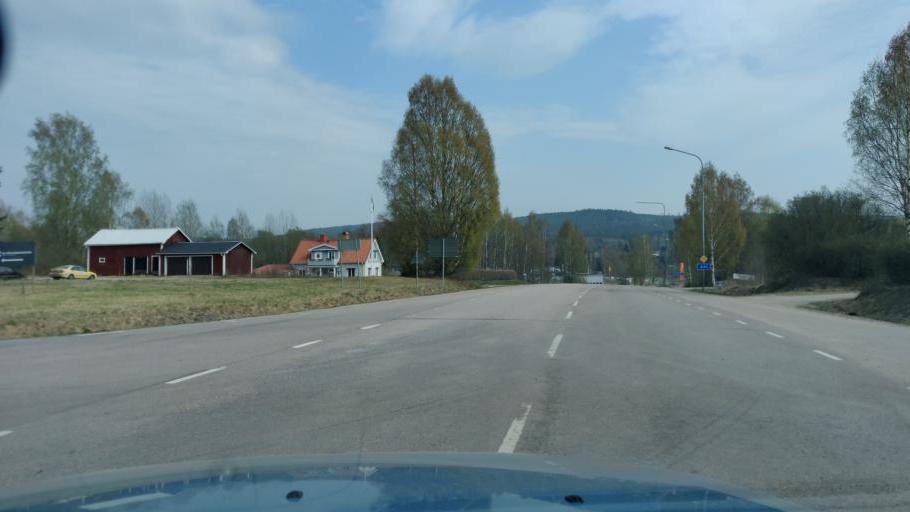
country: SE
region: Vaermland
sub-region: Munkfors Kommun
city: Munkfors
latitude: 59.8303
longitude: 13.5213
